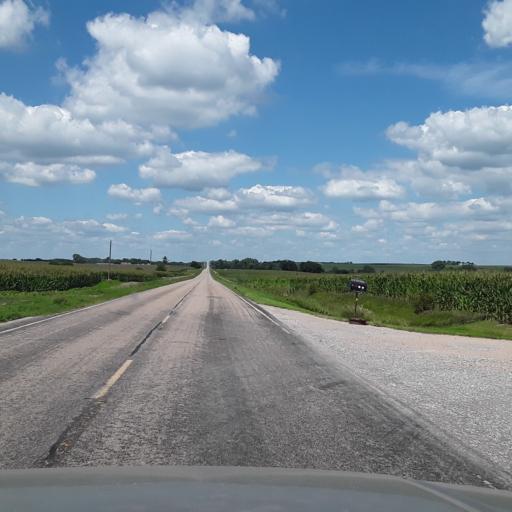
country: US
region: Nebraska
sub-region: Nance County
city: Genoa
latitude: 41.4896
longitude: -97.6963
